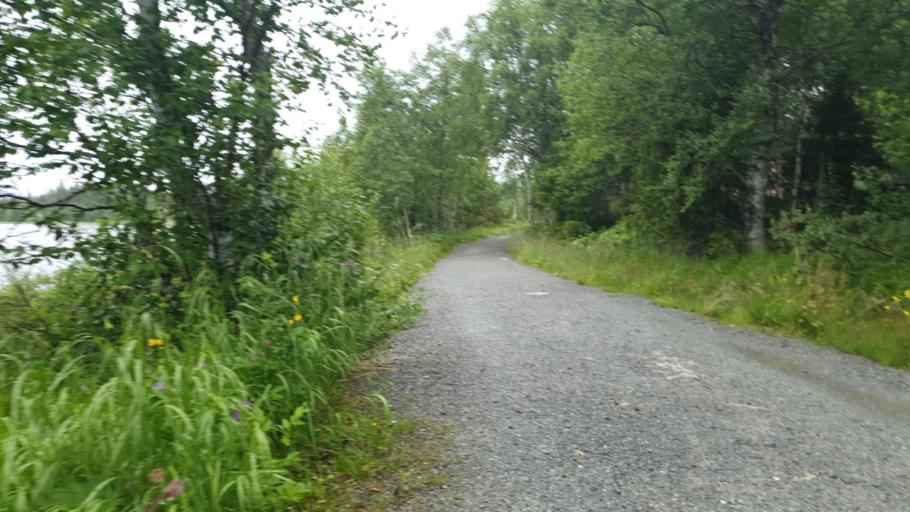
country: NO
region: Oppland
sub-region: Vestre Slidre
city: Slidre
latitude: 61.2310
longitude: 8.9247
